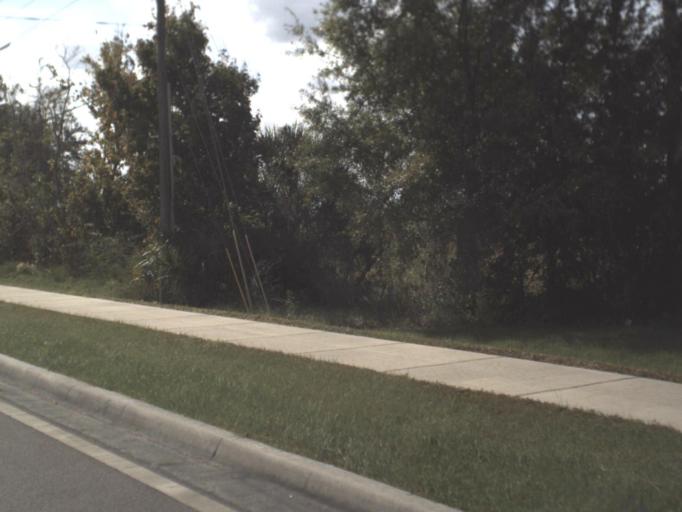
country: US
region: Florida
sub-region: Osceola County
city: Campbell
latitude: 28.2441
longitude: -81.4876
